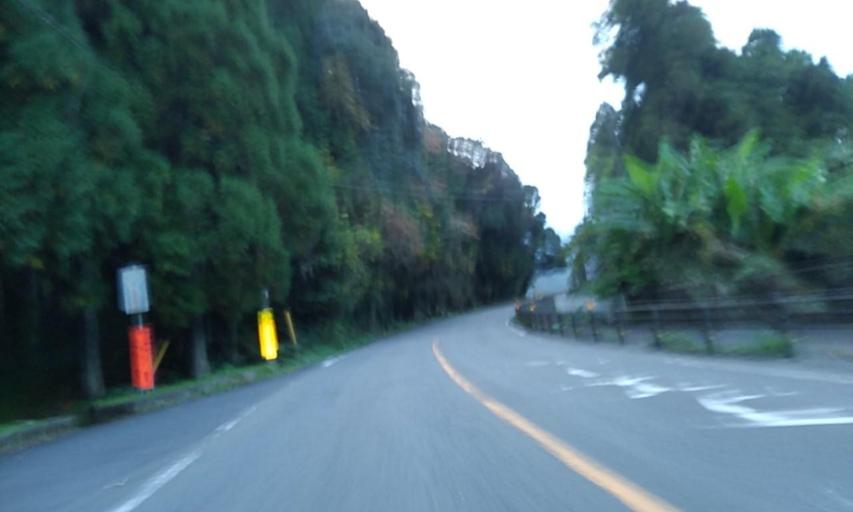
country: JP
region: Wakayama
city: Shingu
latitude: 33.7230
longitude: 135.9666
